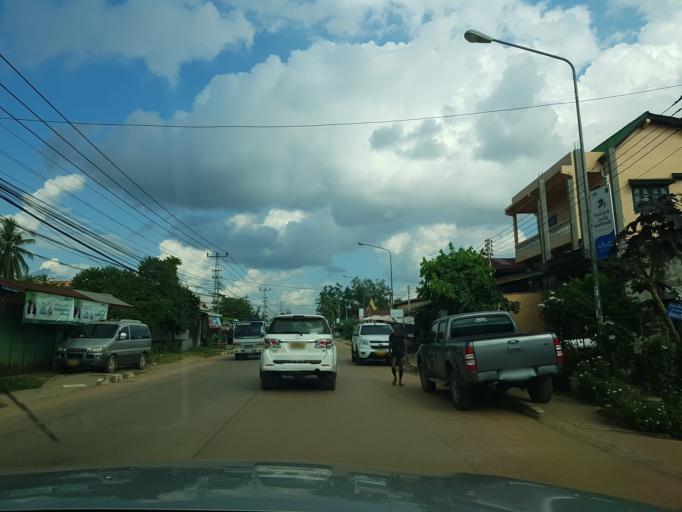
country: TH
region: Nong Khai
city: Si Chiang Mai
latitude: 17.9776
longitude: 102.5319
